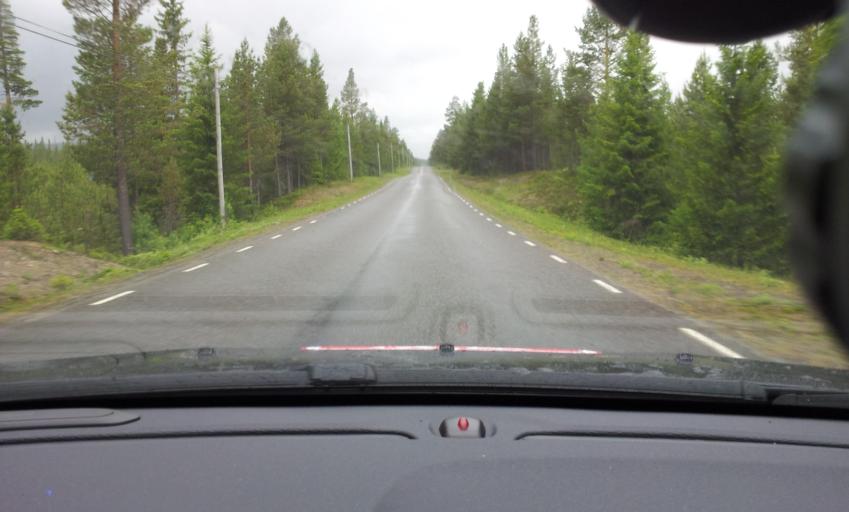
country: SE
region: Jaemtland
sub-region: Are Kommun
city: Are
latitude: 63.1765
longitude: 13.1002
